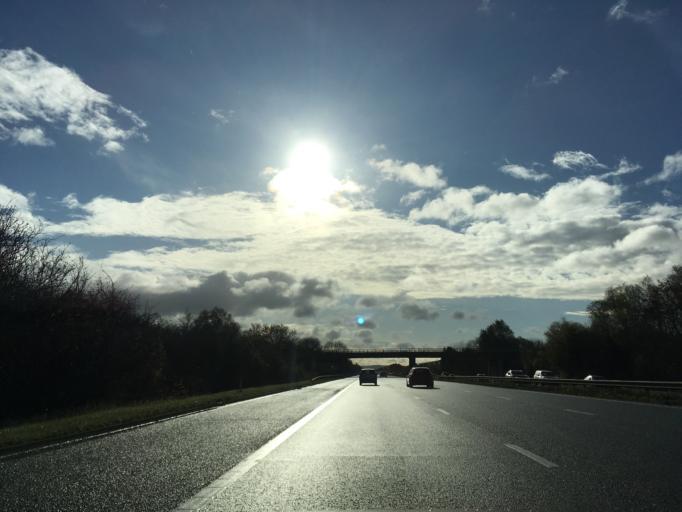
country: GB
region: England
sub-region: Worcestershire
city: Bredon
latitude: 52.0135
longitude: -2.1205
